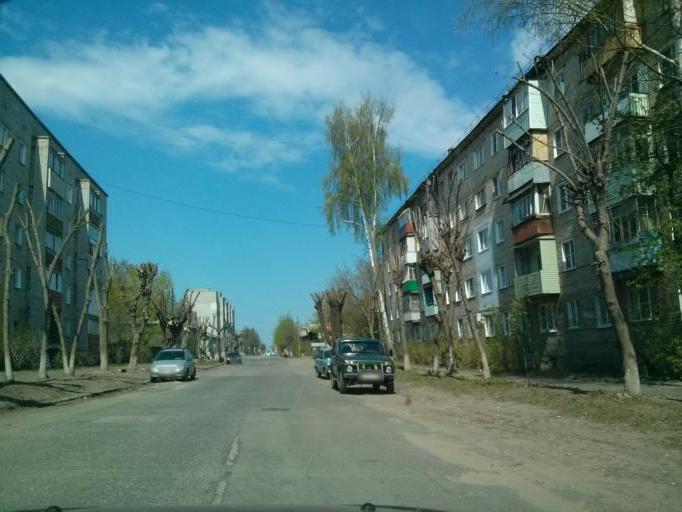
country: RU
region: Vladimir
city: Murom
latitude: 55.5677
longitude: 42.0512
